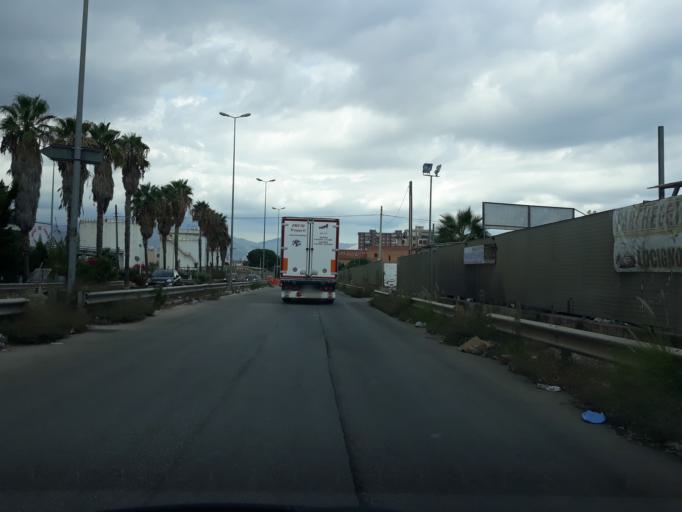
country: IT
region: Sicily
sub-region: Palermo
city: Ciaculli
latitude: 38.0924
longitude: 13.4077
